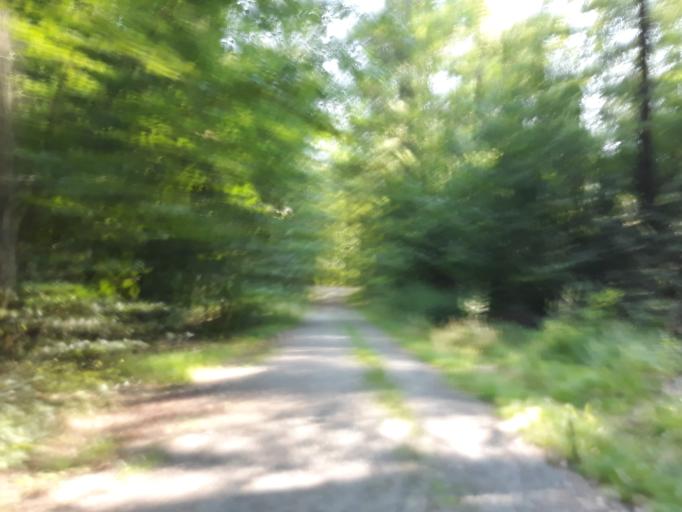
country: DE
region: Baden-Wuerttemberg
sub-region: Regierungsbezirk Stuttgart
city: Schonaich
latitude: 48.6720
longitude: 9.0429
